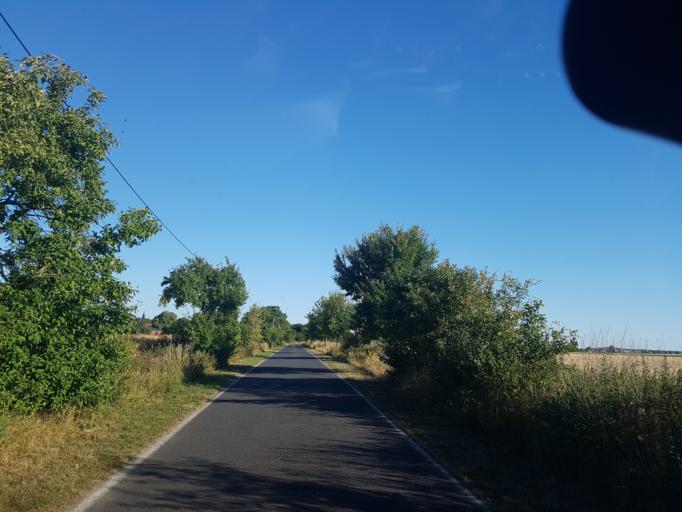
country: DE
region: Brandenburg
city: Juterbog
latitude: 51.9230
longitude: 13.1460
